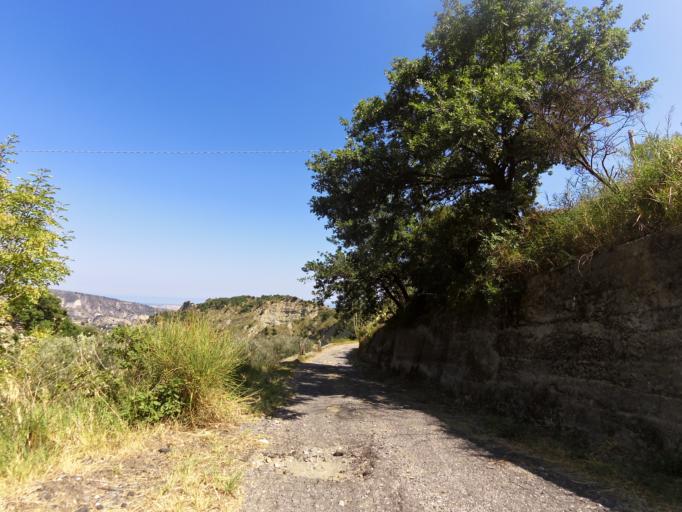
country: IT
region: Calabria
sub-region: Provincia di Reggio Calabria
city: Pazzano
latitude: 38.4655
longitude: 16.4533
